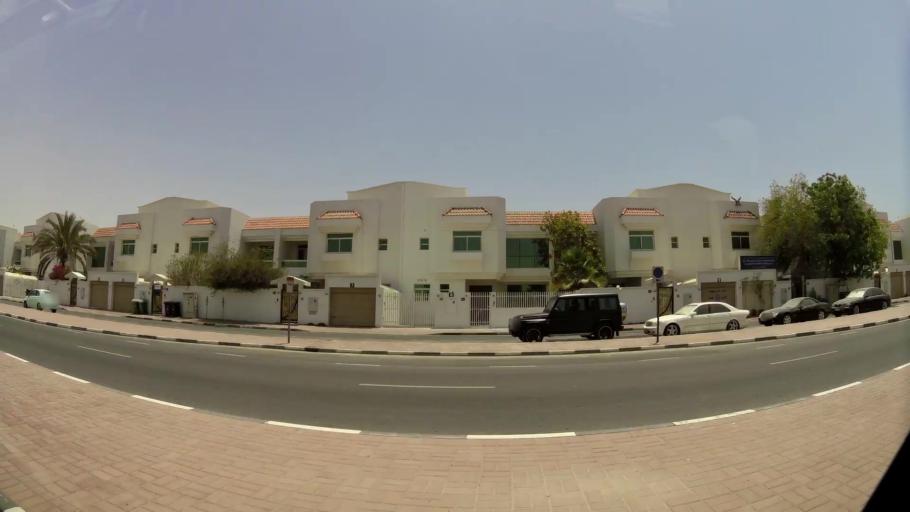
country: AE
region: Dubai
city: Dubai
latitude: 25.1712
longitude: 55.2254
